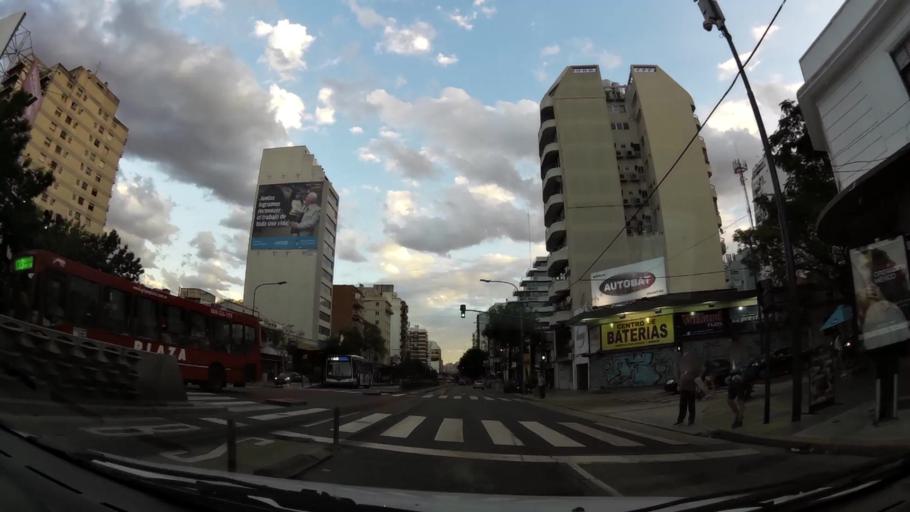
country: AR
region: Buenos Aires
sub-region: Partido de Vicente Lopez
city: Olivos
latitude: -34.5430
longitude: -58.4728
